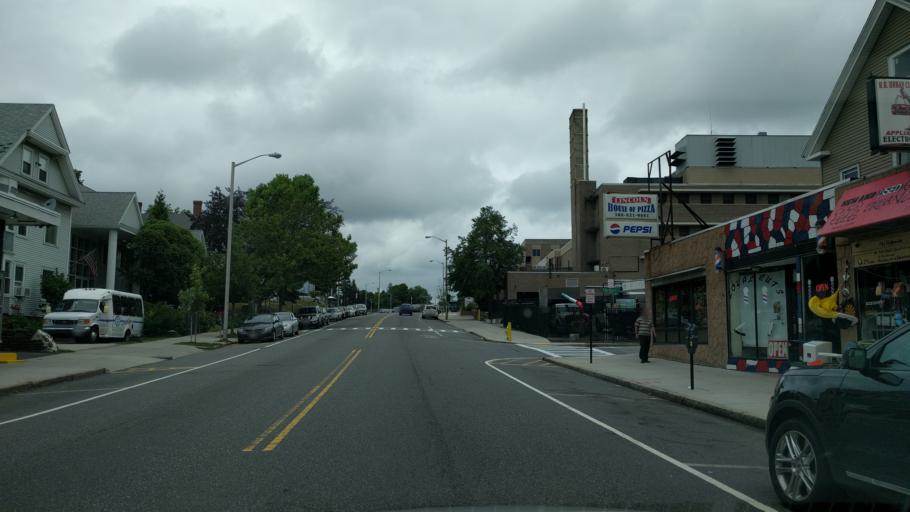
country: US
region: Massachusetts
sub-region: Worcester County
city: Worcester
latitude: 42.2846
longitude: -71.7915
